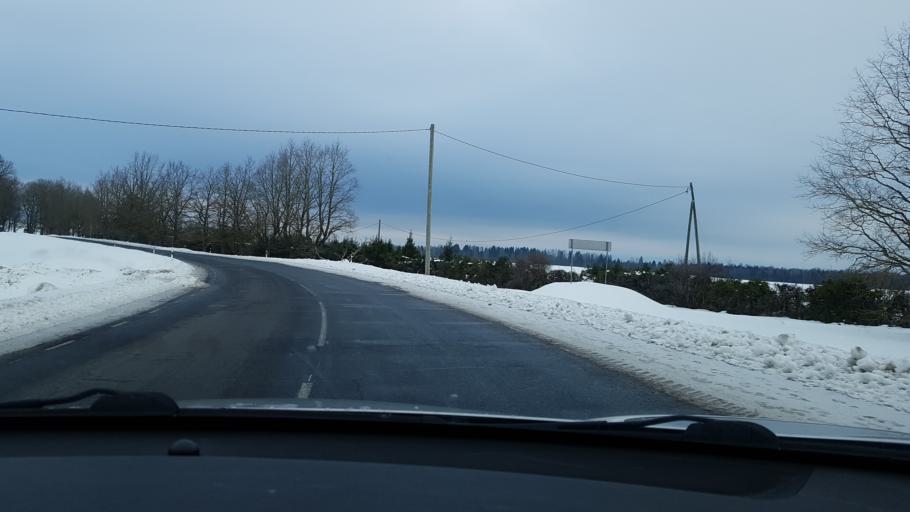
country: EE
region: Jaervamaa
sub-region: Paide linn
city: Paide
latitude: 58.8943
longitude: 25.7131
